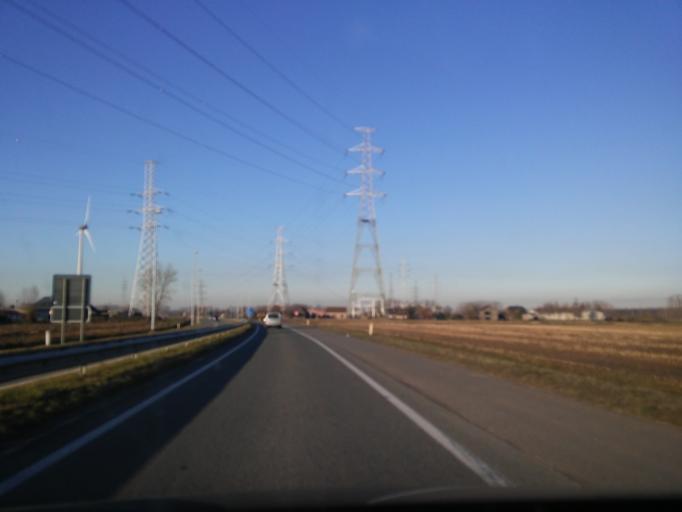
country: BE
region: Flanders
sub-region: Provincie Oost-Vlaanderen
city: Eeklo
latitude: 51.2007
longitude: 3.5350
